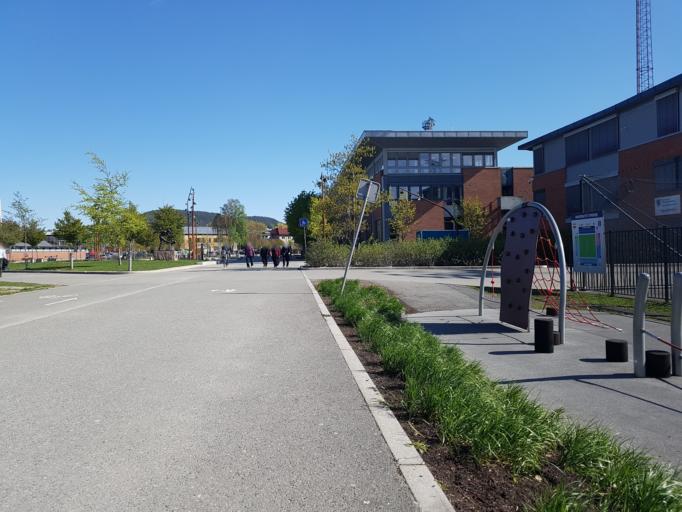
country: NO
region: Buskerud
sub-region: Drammen
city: Drammen
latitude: 59.7355
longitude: 10.2018
